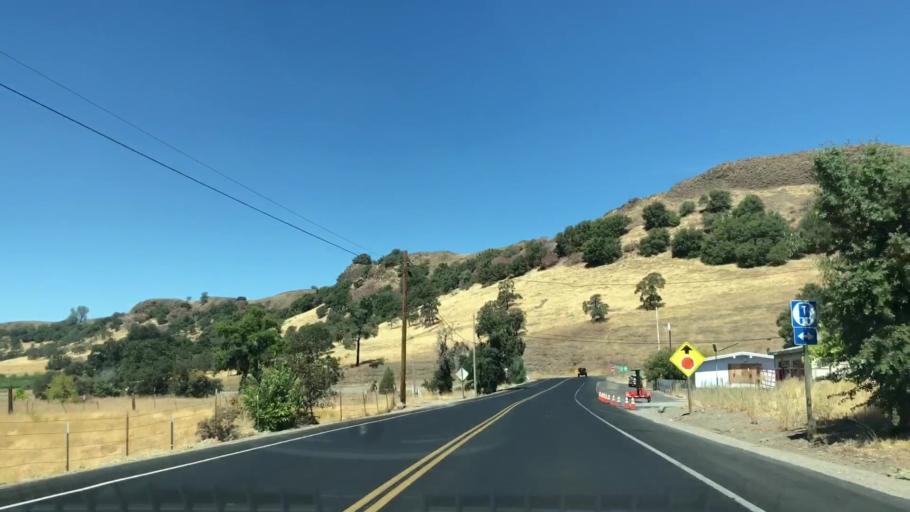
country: US
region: California
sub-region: Tuolumne County
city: Jamestown
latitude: 37.8896
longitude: -120.4873
